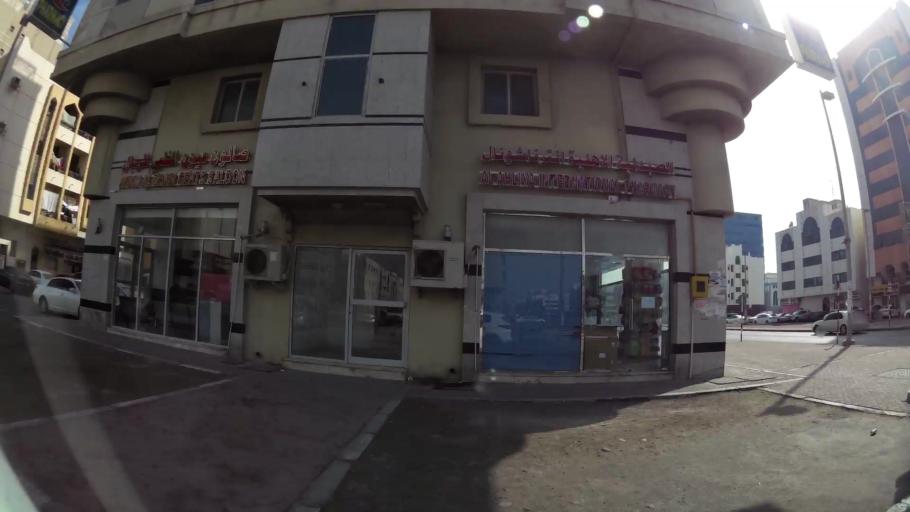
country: AE
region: Abu Dhabi
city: Abu Dhabi
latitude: 24.3264
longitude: 54.5356
